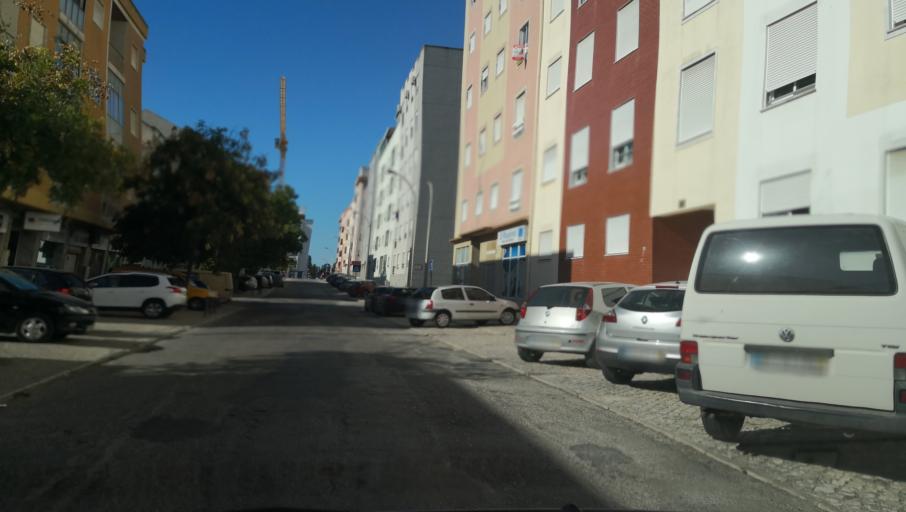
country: PT
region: Setubal
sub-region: Setubal
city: Setubal
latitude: 38.5282
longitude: -8.8741
